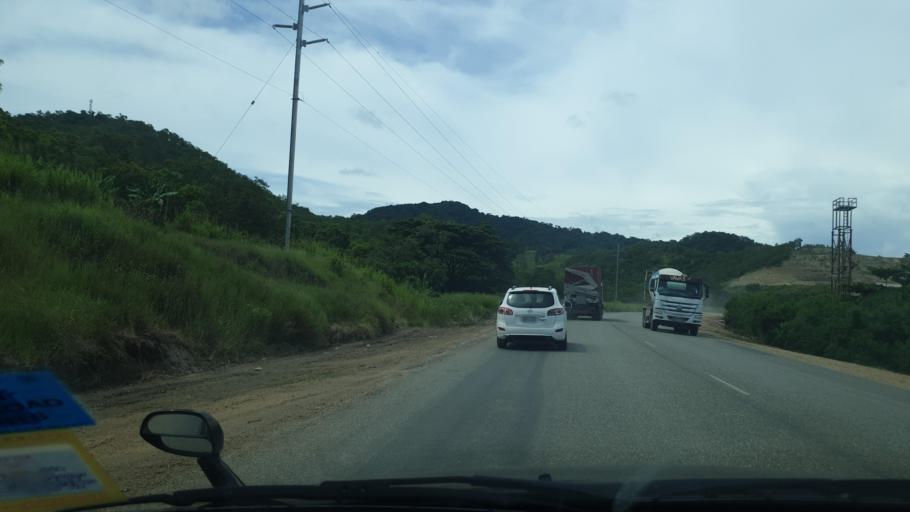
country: PG
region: National Capital
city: Port Moresby
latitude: -9.4181
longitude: 147.0996
